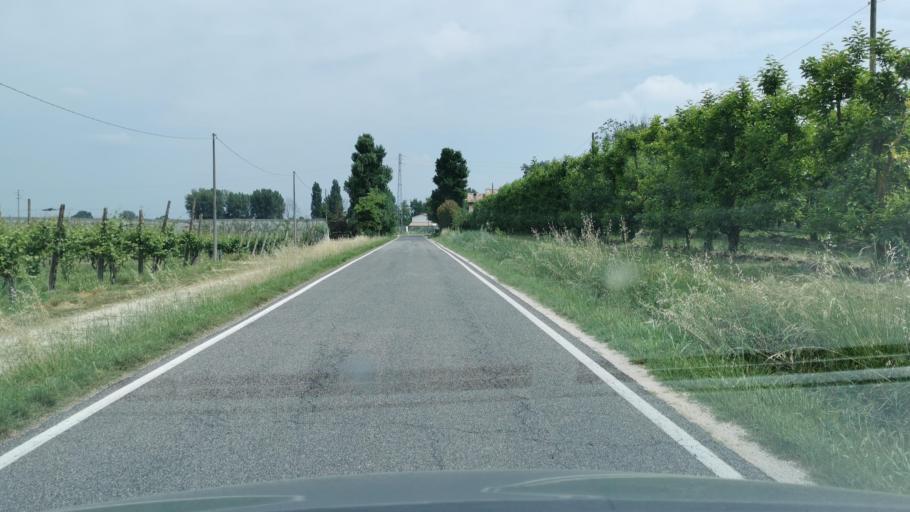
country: IT
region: Emilia-Romagna
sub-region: Provincia di Ravenna
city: Russi
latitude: 44.3961
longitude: 12.0165
